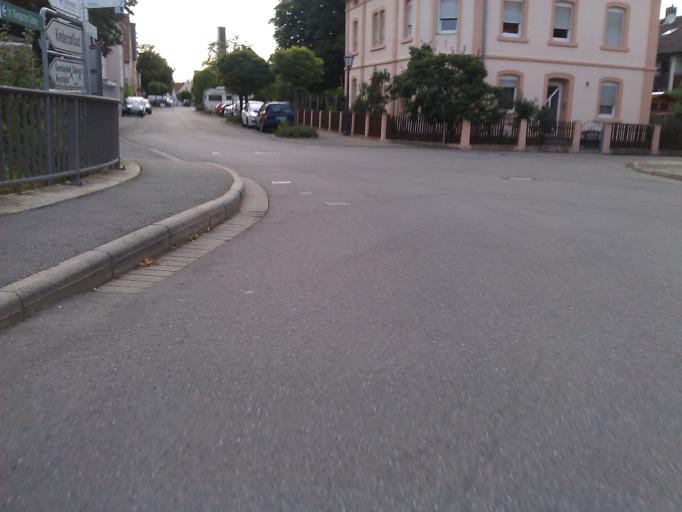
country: DE
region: Baden-Wuerttemberg
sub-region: Regierungsbezirk Stuttgart
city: Untereisesheim
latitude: 49.2326
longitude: 9.1940
